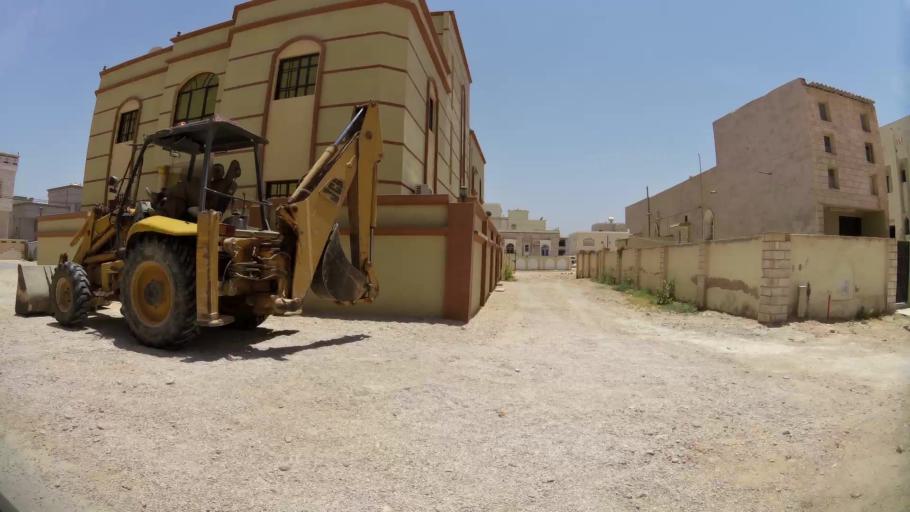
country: OM
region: Zufar
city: Salalah
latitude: 17.0721
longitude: 54.1525
